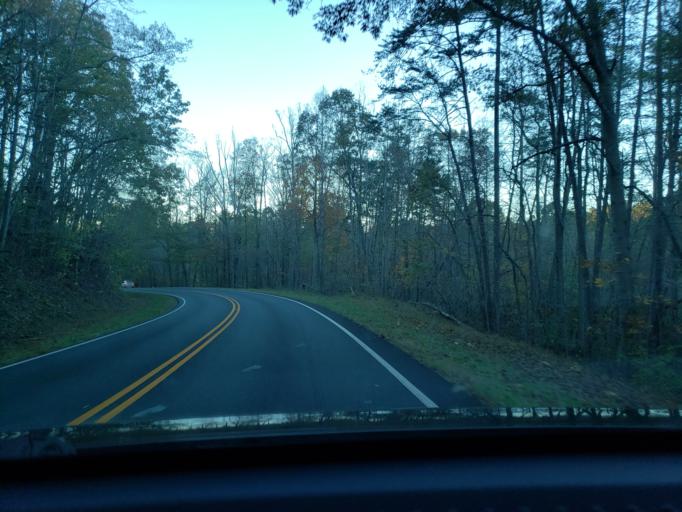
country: US
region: North Carolina
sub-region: Stokes County
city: Danbury
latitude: 36.3809
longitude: -80.1859
